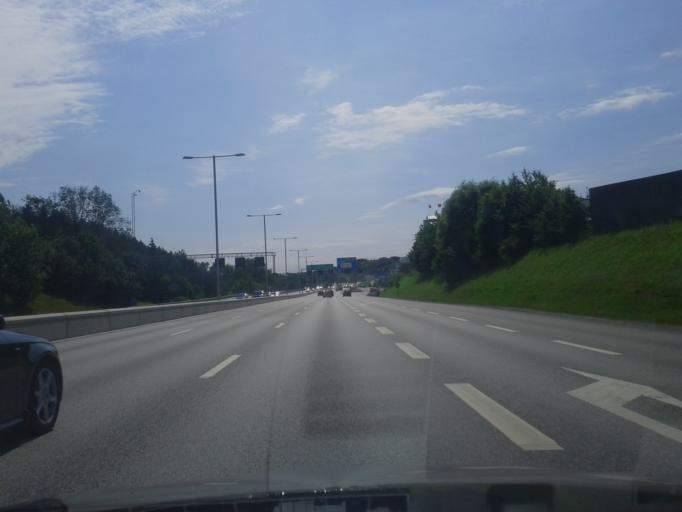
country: SE
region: Stockholm
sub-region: Solna Kommun
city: Solna
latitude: 59.3821
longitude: 18.0083
